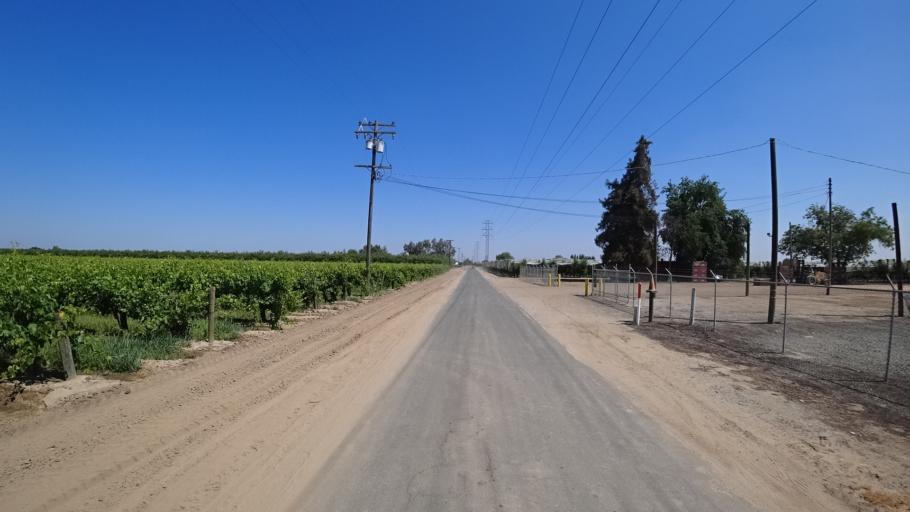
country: US
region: California
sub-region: Fresno County
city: Kingsburg
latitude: 36.4532
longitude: -119.5914
